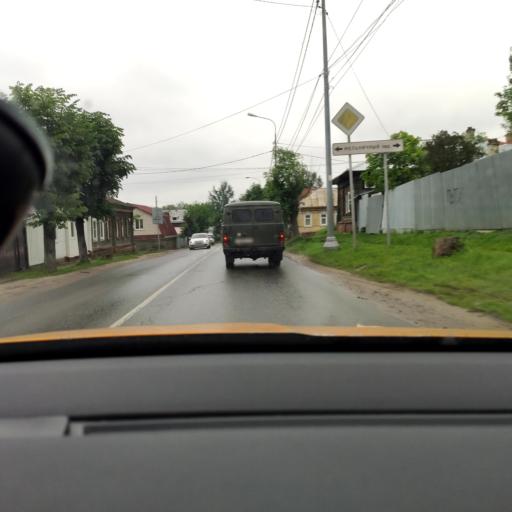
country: RU
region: Moskovskaya
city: Serpukhov
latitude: 54.9157
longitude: 37.3949
